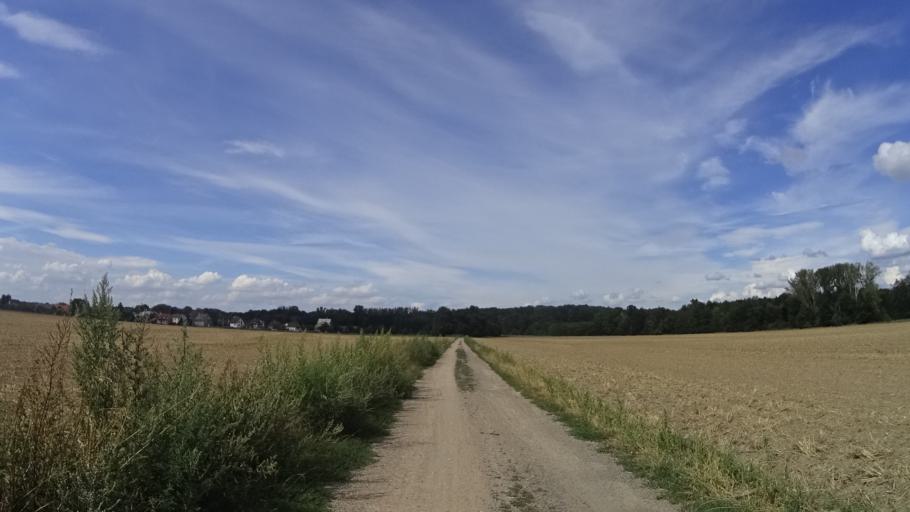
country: CZ
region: Olomoucky
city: Skrben
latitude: 49.6654
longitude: 17.1781
